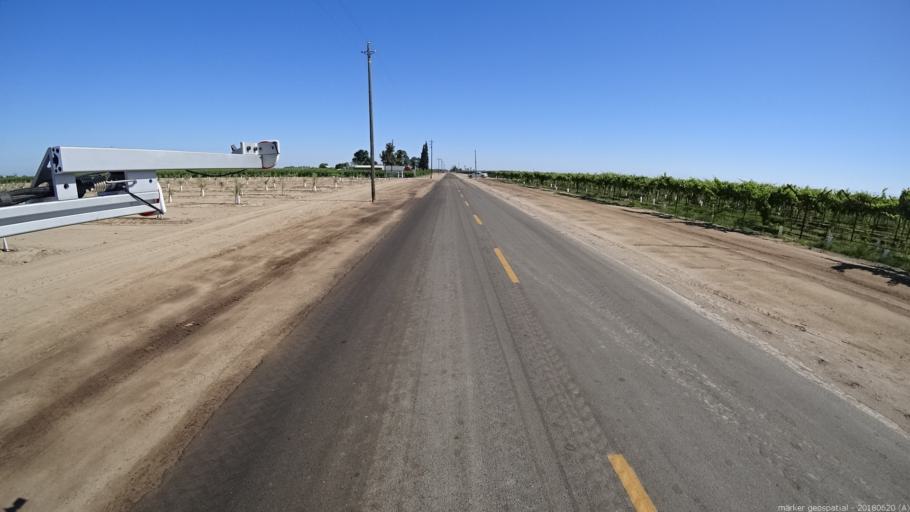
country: US
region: California
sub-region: Fresno County
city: Biola
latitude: 36.8613
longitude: -120.0374
